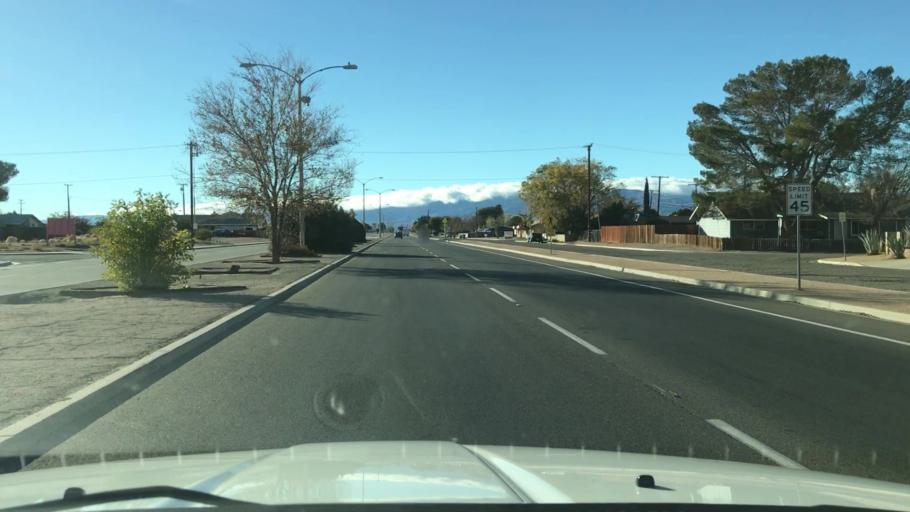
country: US
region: California
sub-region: Kern County
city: California City
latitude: 35.1258
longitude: -117.9864
